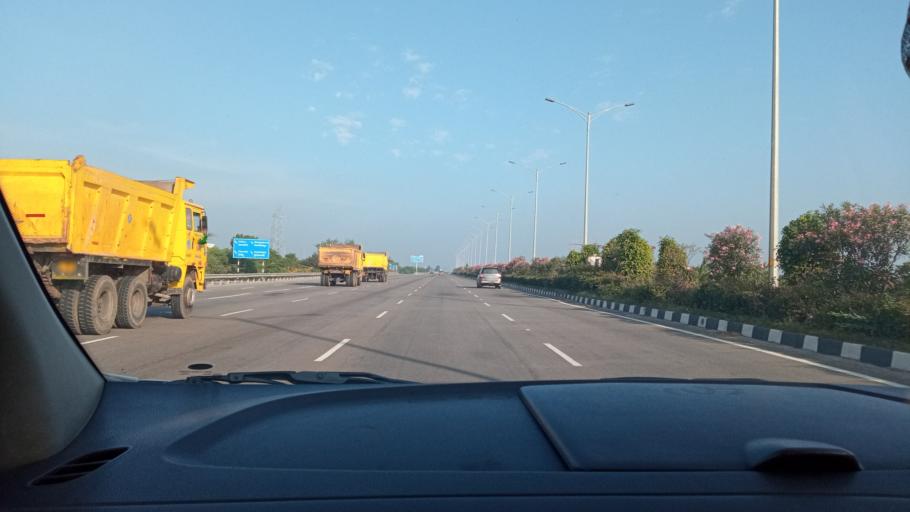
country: IN
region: Telangana
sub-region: Hyderabad
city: Hyderabad
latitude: 17.3430
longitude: 78.3637
